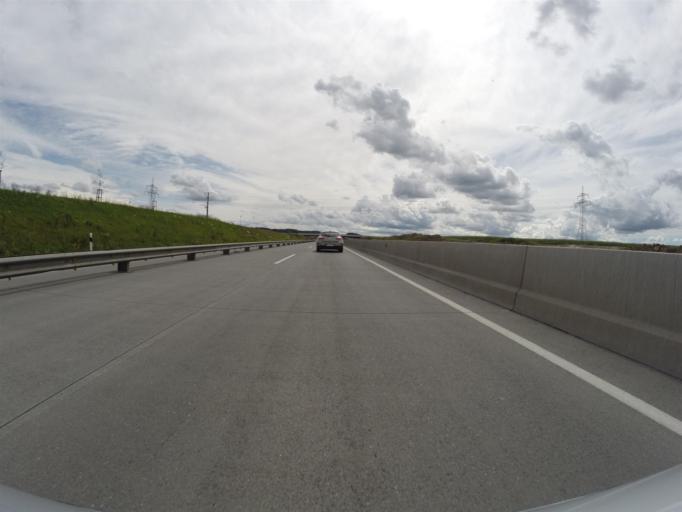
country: DE
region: Thuringia
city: Gorkwitz
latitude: 50.5817
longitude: 11.7778
